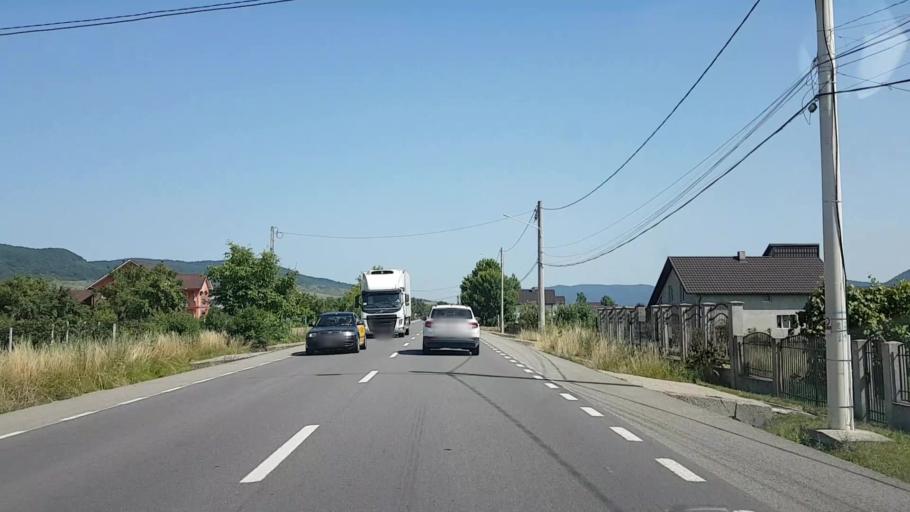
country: RO
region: Bistrita-Nasaud
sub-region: Comuna Sieu-Magherus
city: Sieu-Magherus
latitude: 47.0982
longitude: 24.3645
